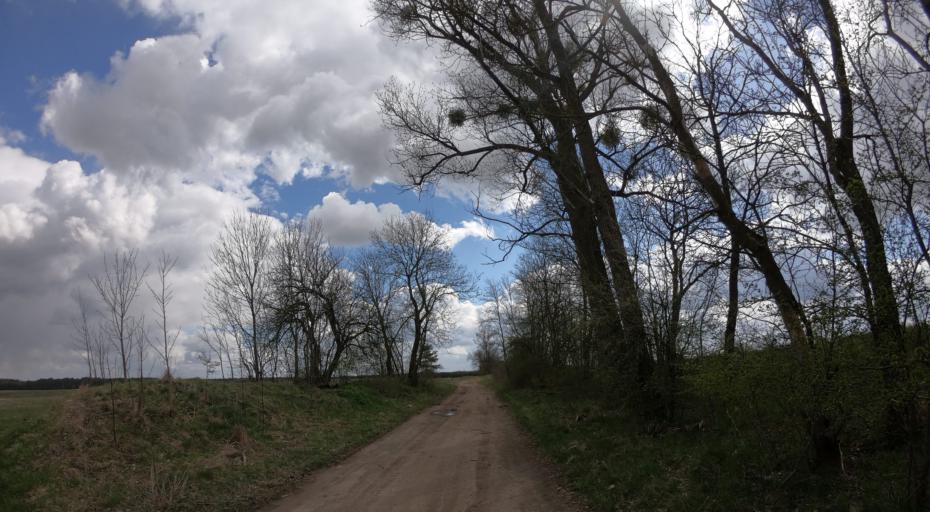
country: PL
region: West Pomeranian Voivodeship
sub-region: Powiat drawski
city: Drawsko Pomorskie
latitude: 53.5608
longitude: 15.8542
